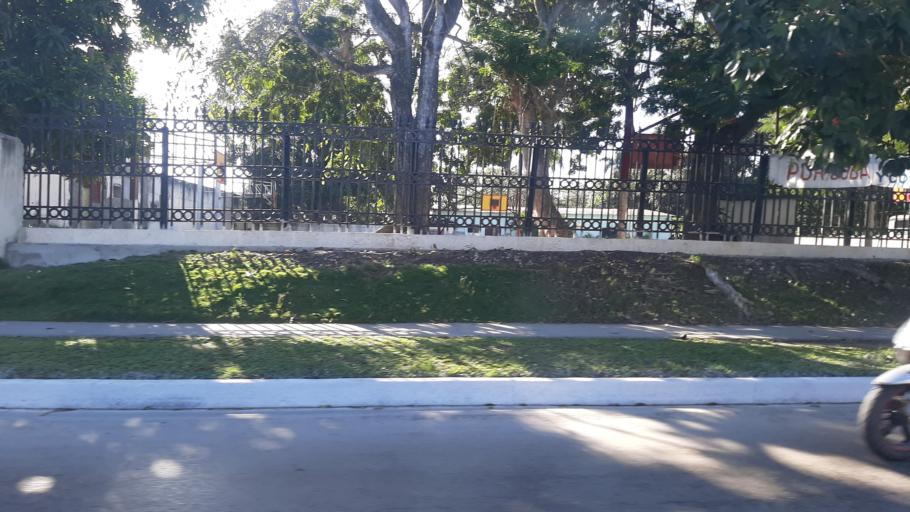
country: CU
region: Villa Clara
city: Santa Clara
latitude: 22.4118
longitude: -79.9574
